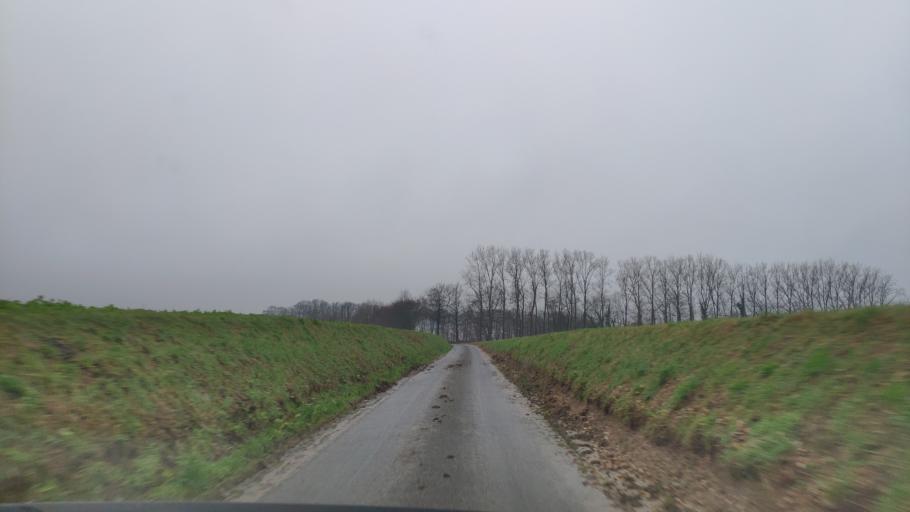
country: FR
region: Haute-Normandie
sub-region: Departement de la Seine-Maritime
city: Neville
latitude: 49.7932
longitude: 0.7050
